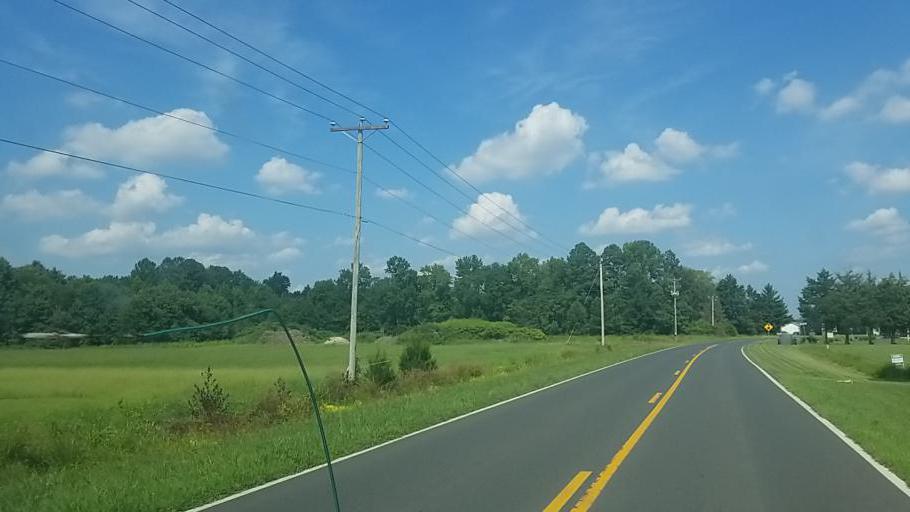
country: US
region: Maryland
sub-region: Wicomico County
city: Fruitland
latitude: 38.3142
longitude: -75.6364
